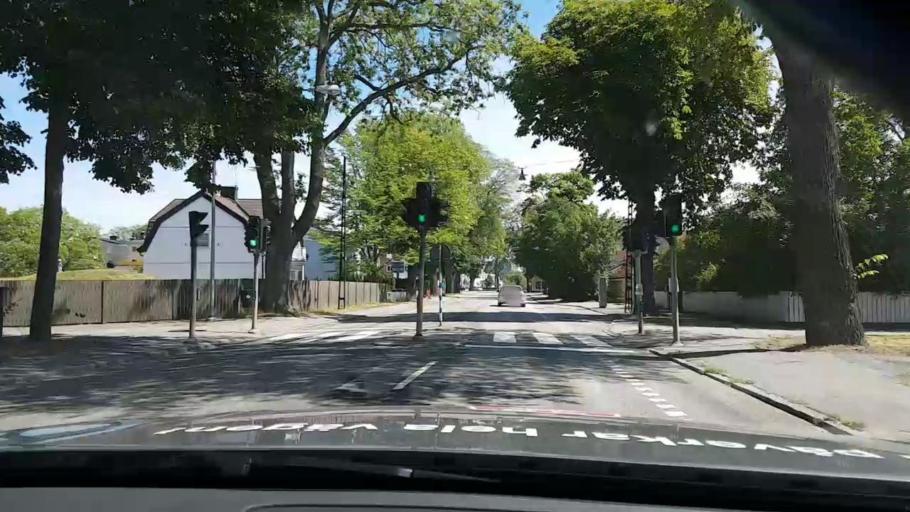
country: SE
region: Kalmar
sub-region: Vasterviks Kommun
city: Vaestervik
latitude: 57.7575
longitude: 16.6262
